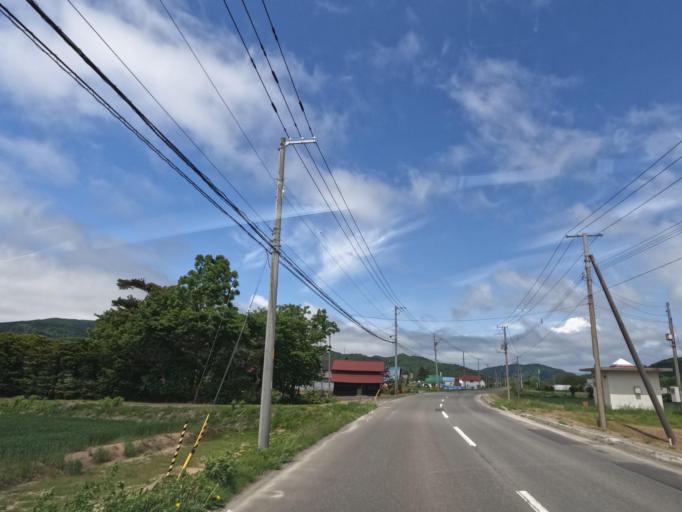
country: JP
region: Hokkaido
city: Tobetsu
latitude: 43.2784
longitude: 141.5346
